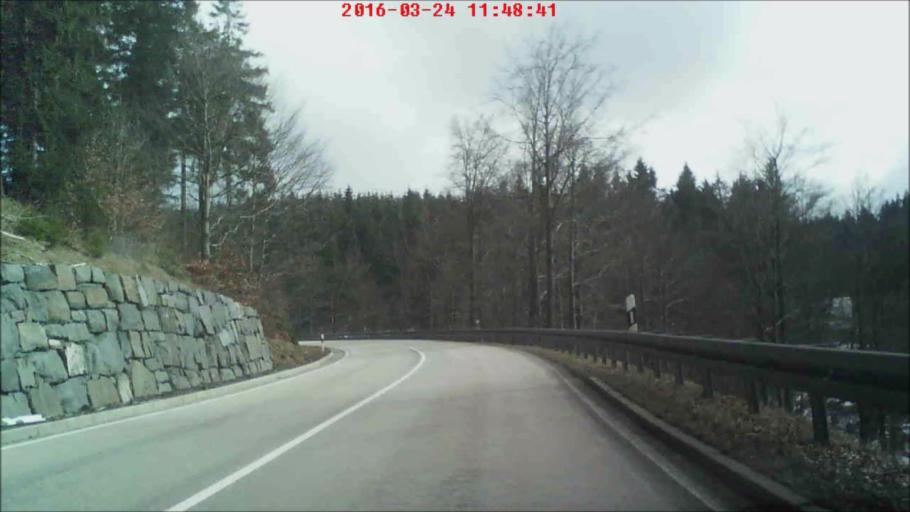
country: DE
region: Thuringia
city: Steinheid
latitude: 50.4655
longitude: 11.0300
